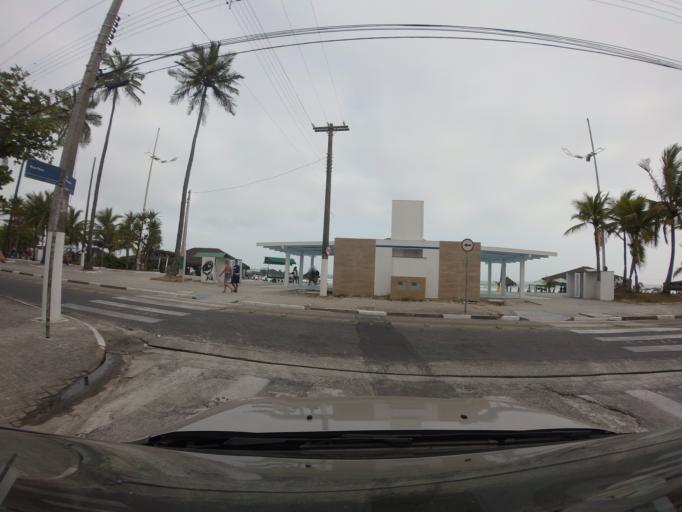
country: BR
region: Sao Paulo
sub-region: Guaruja
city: Guaruja
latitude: -23.9885
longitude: -46.2372
